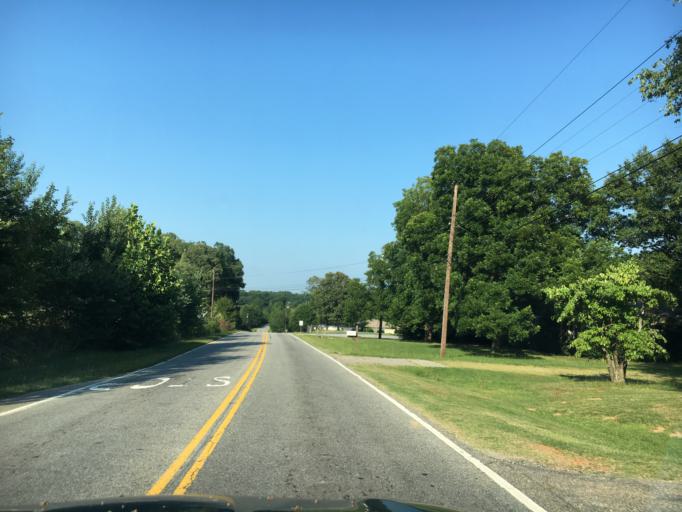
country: US
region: South Carolina
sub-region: Spartanburg County
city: Duncan
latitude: 34.8916
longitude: -82.1401
